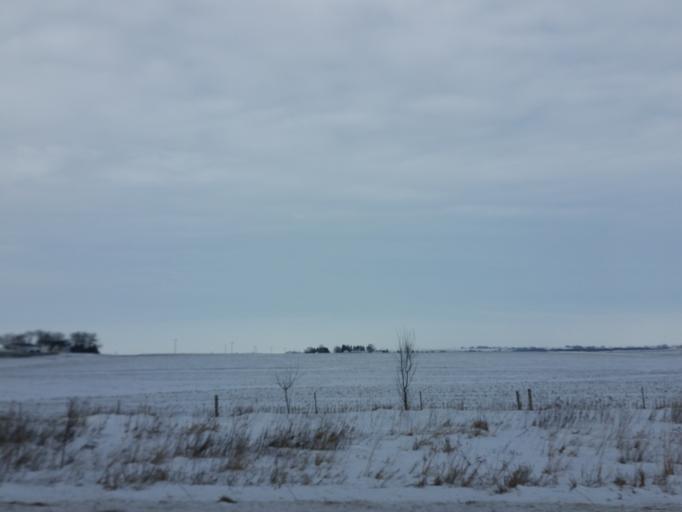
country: US
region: Iowa
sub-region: Delaware County
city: Manchester
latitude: 42.4644
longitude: -91.5772
